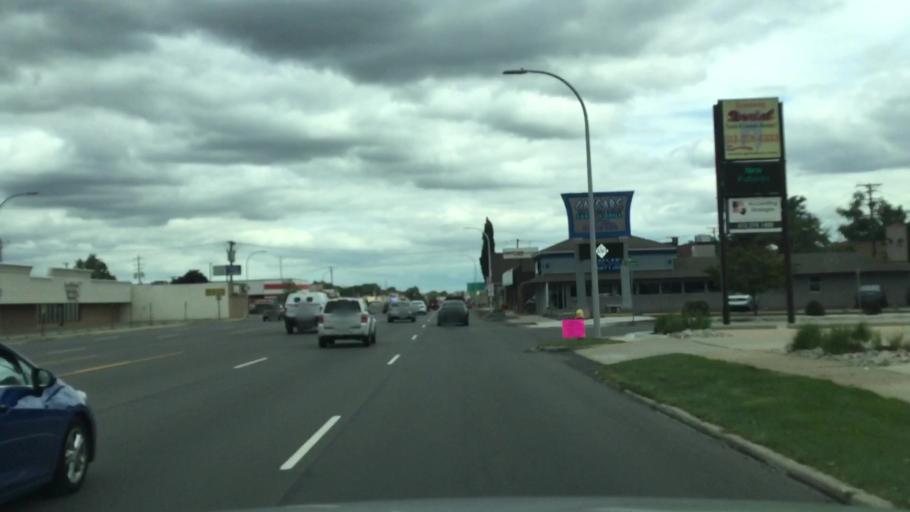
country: US
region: Michigan
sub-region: Wayne County
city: Dearborn Heights
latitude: 42.3268
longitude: -83.2777
